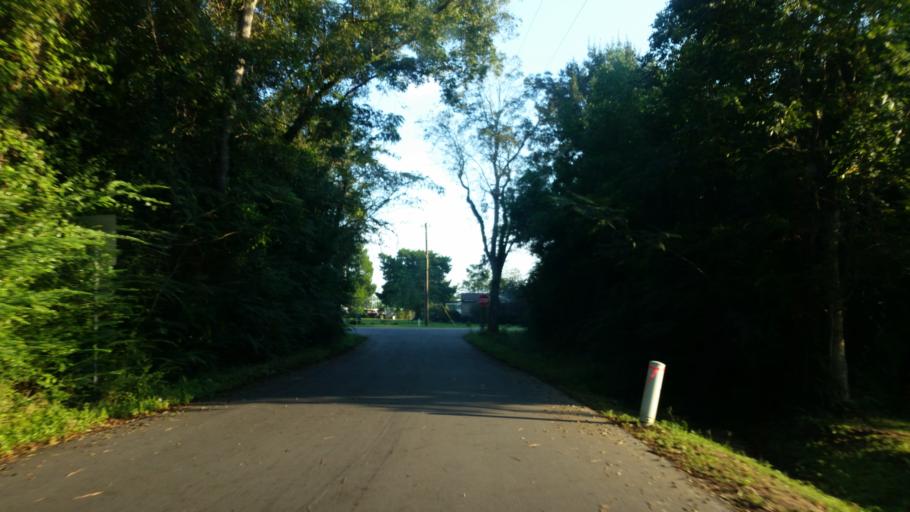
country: US
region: Florida
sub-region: Santa Rosa County
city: East Milton
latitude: 30.6297
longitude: -87.0191
